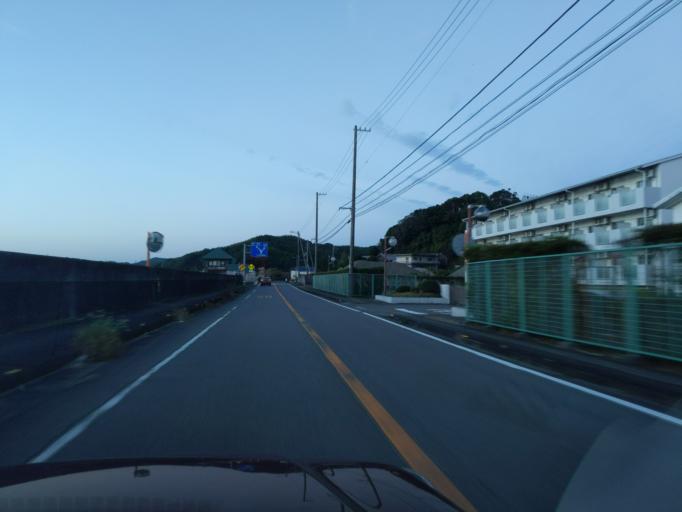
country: JP
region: Tokushima
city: Anan
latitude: 33.8627
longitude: 134.6311
